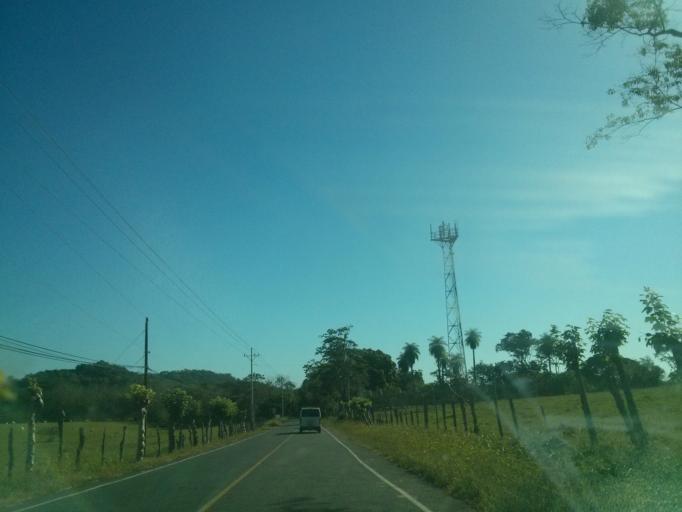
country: CR
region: Puntarenas
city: Paquera
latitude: 9.7027
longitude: -85.0529
